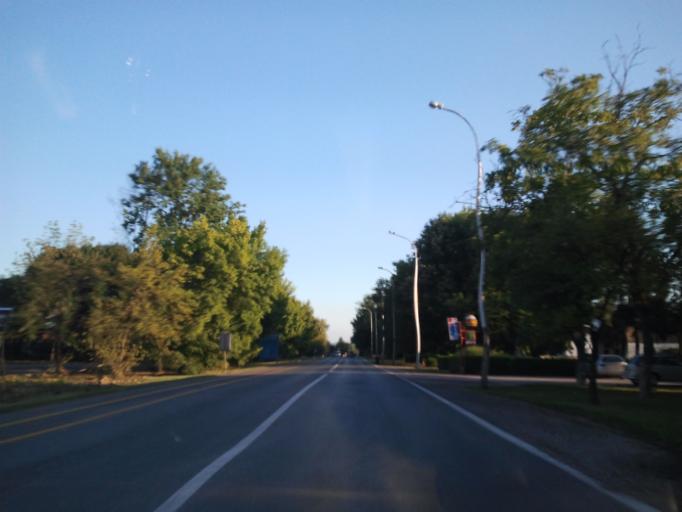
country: HR
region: Sisacko-Moslavacka
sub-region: Grad Sisak
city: Sisak
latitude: 45.4577
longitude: 16.3714
